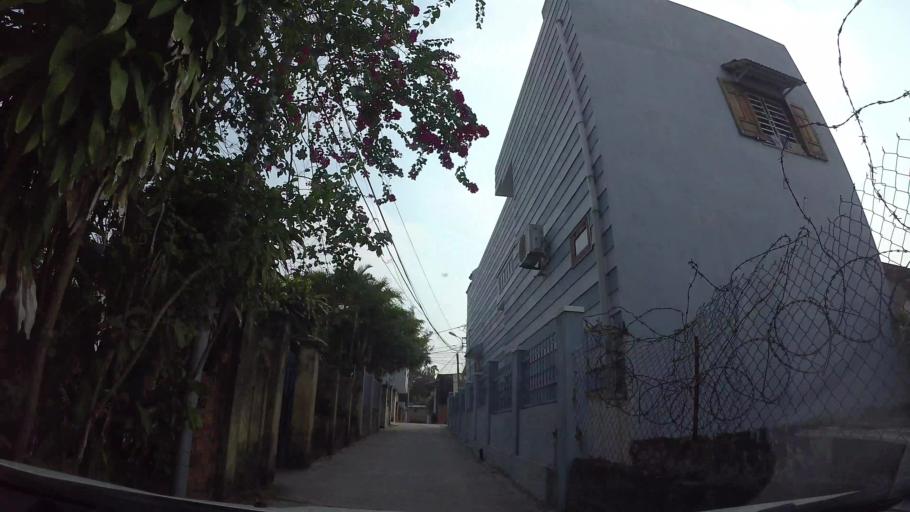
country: VN
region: Da Nang
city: Ngu Hanh Son
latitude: 16.0269
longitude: 108.2450
